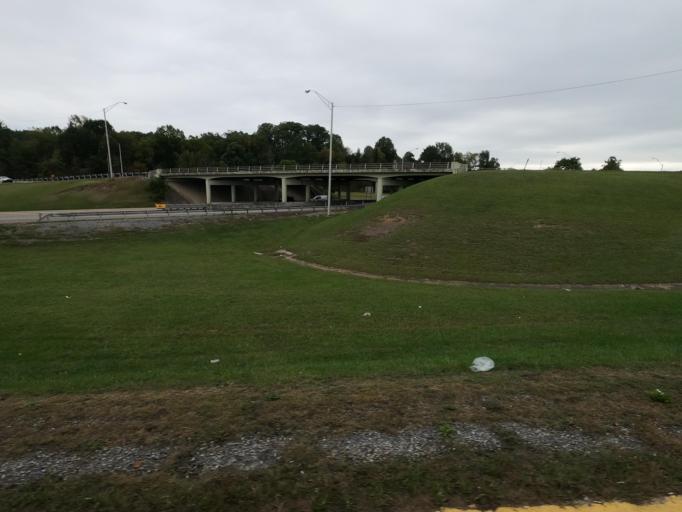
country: US
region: Tennessee
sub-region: Sullivan County
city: Bloomingdale
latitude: 36.5445
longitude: -82.5096
